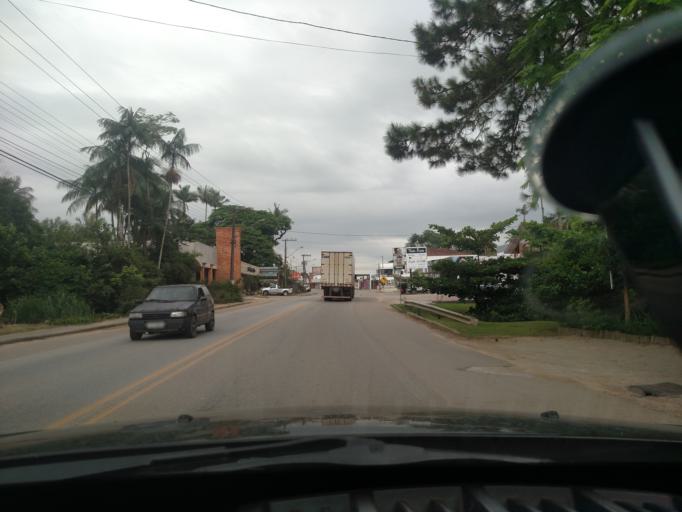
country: BR
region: Santa Catarina
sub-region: Gaspar
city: Gaspar
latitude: -26.9040
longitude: -48.8345
